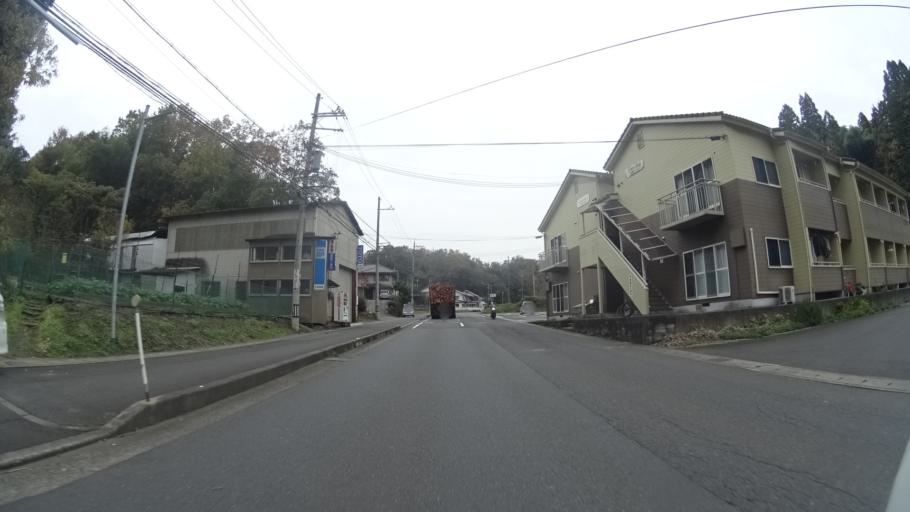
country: JP
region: Kyoto
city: Maizuru
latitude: 35.4909
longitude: 135.4366
